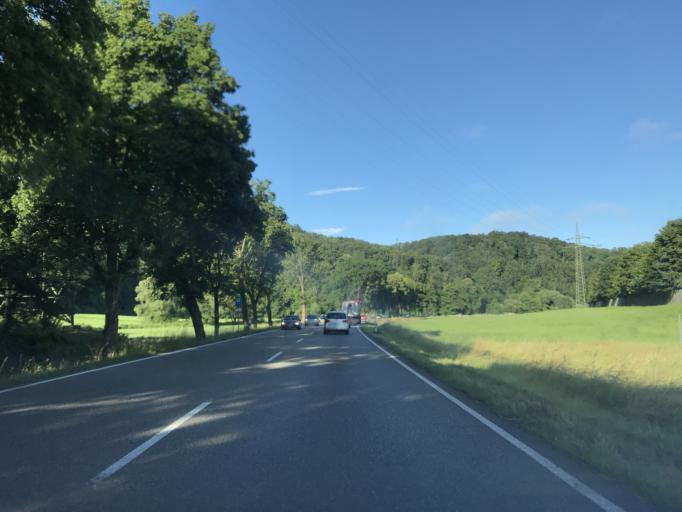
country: DE
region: Baden-Wuerttemberg
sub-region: Freiburg Region
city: Steinen
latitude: 47.6382
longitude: 7.7384
